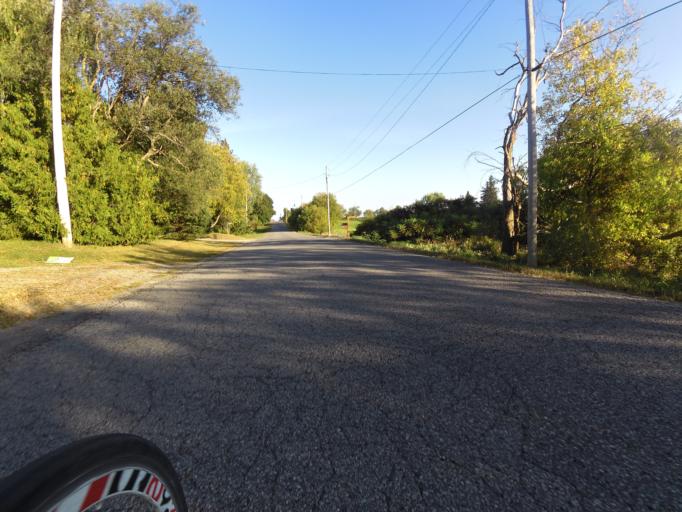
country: CA
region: Ontario
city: Bells Corners
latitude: 45.2278
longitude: -75.7300
